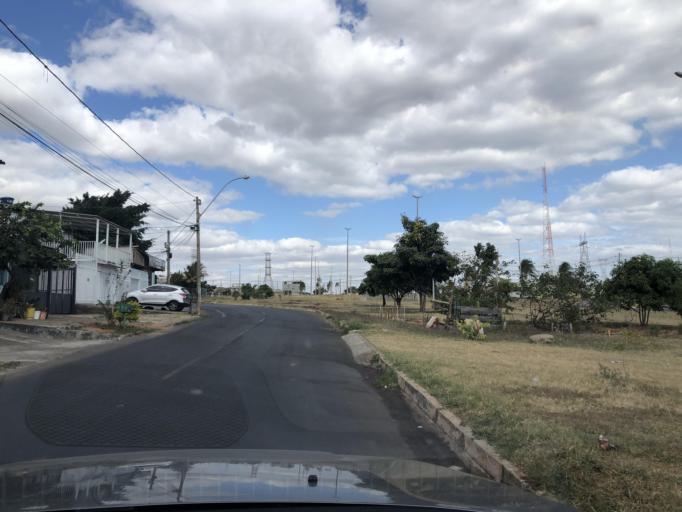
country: BR
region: Federal District
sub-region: Brasilia
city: Brasilia
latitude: -15.8874
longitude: -48.1292
